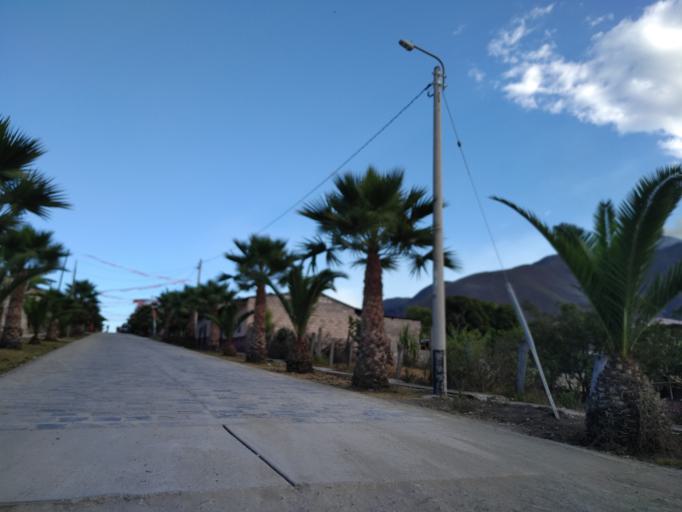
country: PE
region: Amazonas
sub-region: Provincia de Luya
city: Tingo
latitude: -6.3710
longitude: -77.9105
